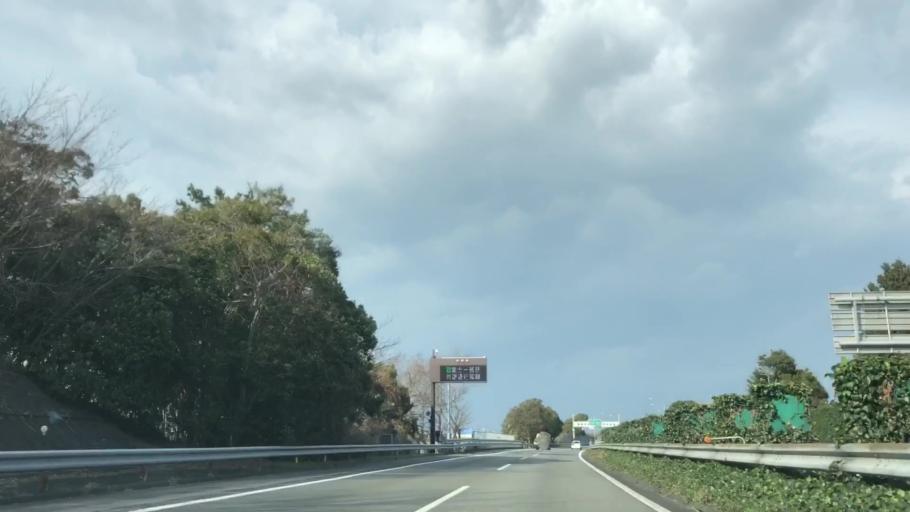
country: JP
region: Shizuoka
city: Shimada
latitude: 34.7860
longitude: 138.2306
